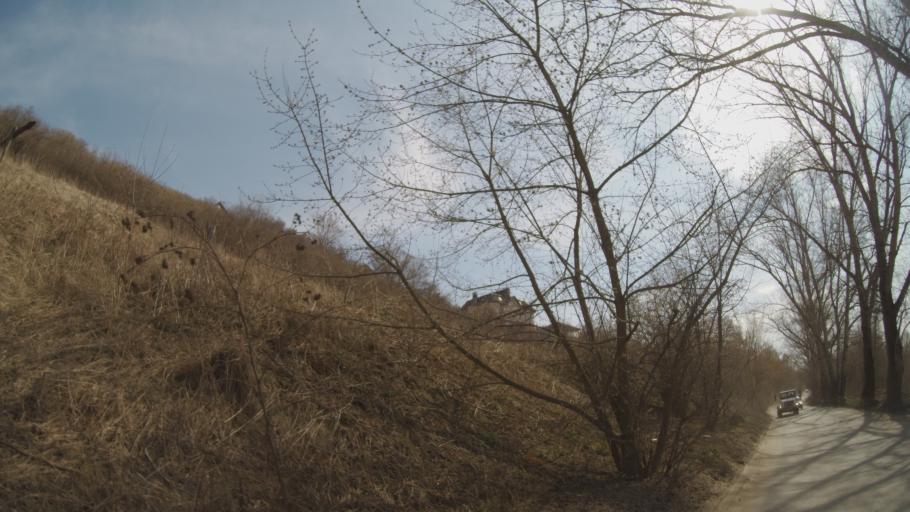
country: RU
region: Nizjnij Novgorod
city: Vyyezdnoye
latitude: 55.3907
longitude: 43.8084
